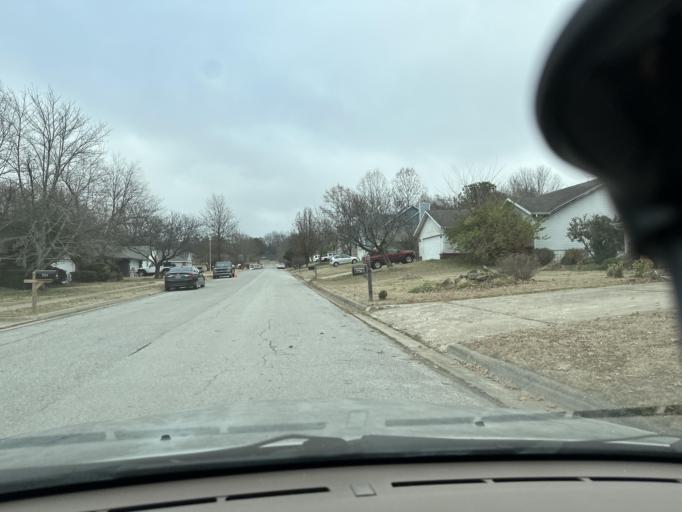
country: US
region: Arkansas
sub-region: Washington County
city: Fayetteville
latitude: 36.0841
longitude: -94.1210
